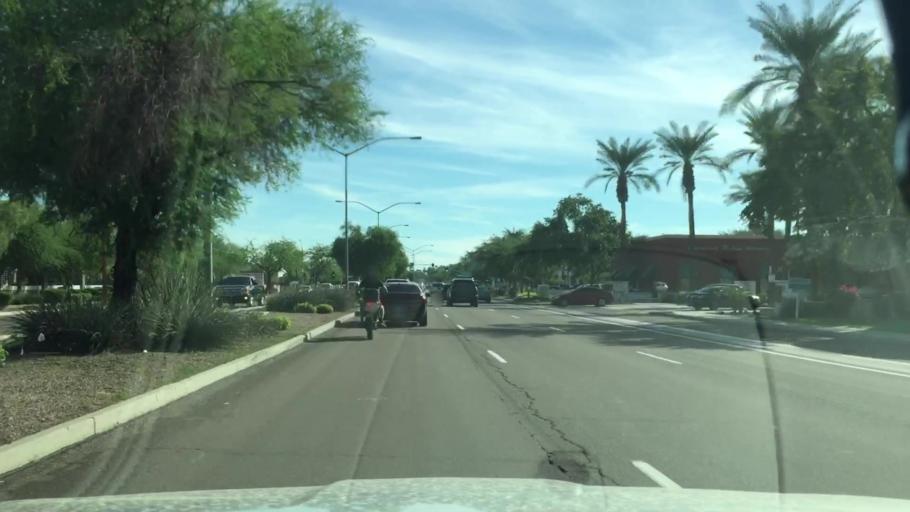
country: US
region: Arizona
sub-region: Maricopa County
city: Gilbert
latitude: 33.3845
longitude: -111.7540
